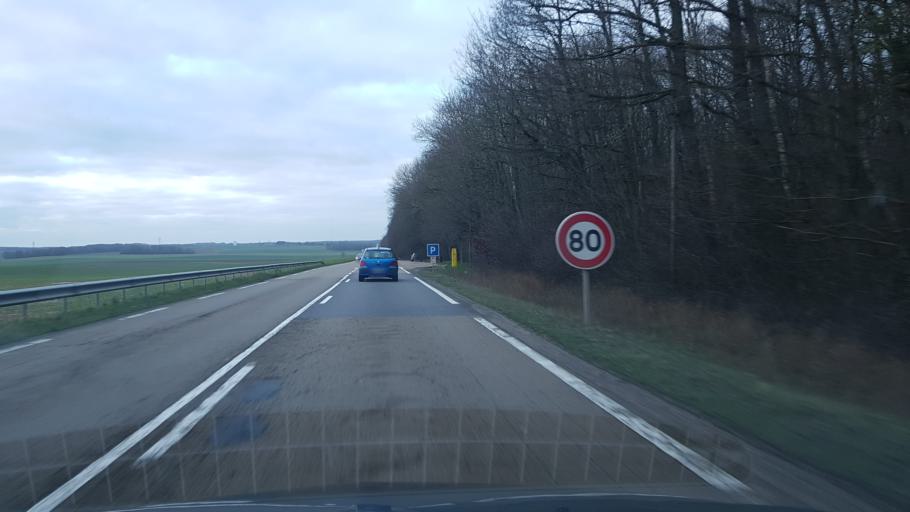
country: FR
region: Champagne-Ardenne
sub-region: Departement de la Marne
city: Esternay
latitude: 48.7199
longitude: 3.5354
